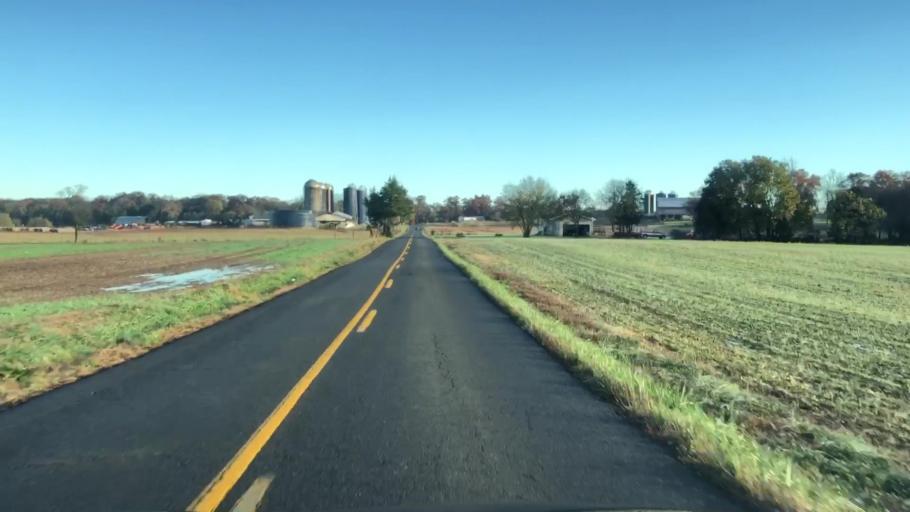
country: US
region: Virginia
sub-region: Prince William County
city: Nokesville
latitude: 38.6738
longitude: -77.6707
